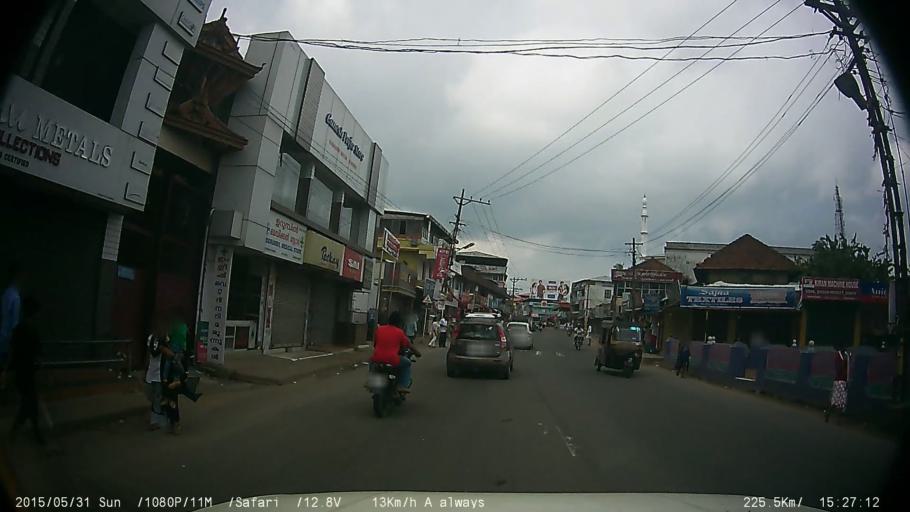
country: IN
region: Kerala
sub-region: Wayanad
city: Panamaram
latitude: 11.6630
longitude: 76.2573
